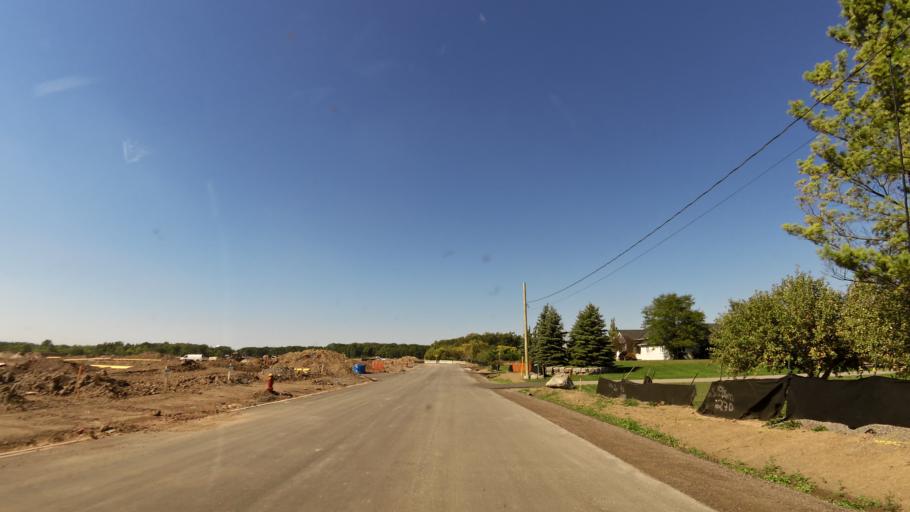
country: CA
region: Ontario
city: Oakville
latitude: 43.4949
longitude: -79.7148
